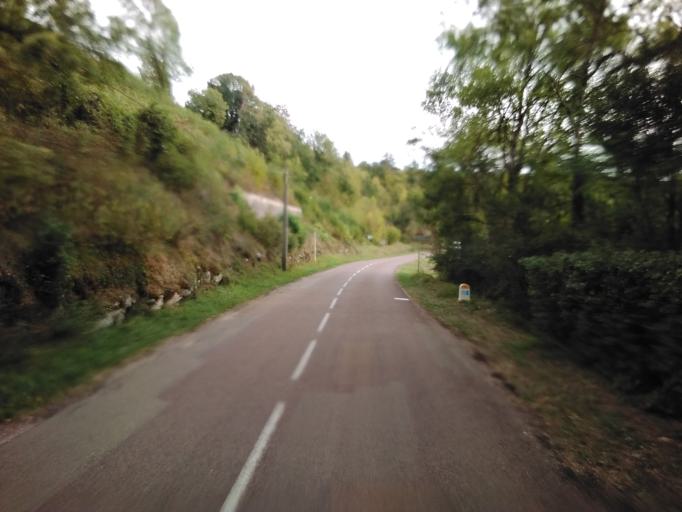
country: FR
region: Champagne-Ardenne
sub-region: Departement de l'Aube
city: Les Riceys
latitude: 47.9343
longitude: 4.3554
